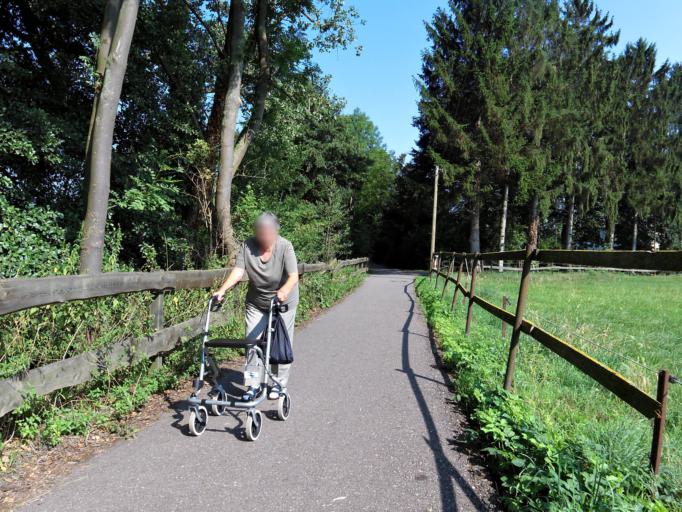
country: DE
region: North Rhine-Westphalia
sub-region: Regierungsbezirk Koln
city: Linnich
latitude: 51.0065
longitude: 6.2418
